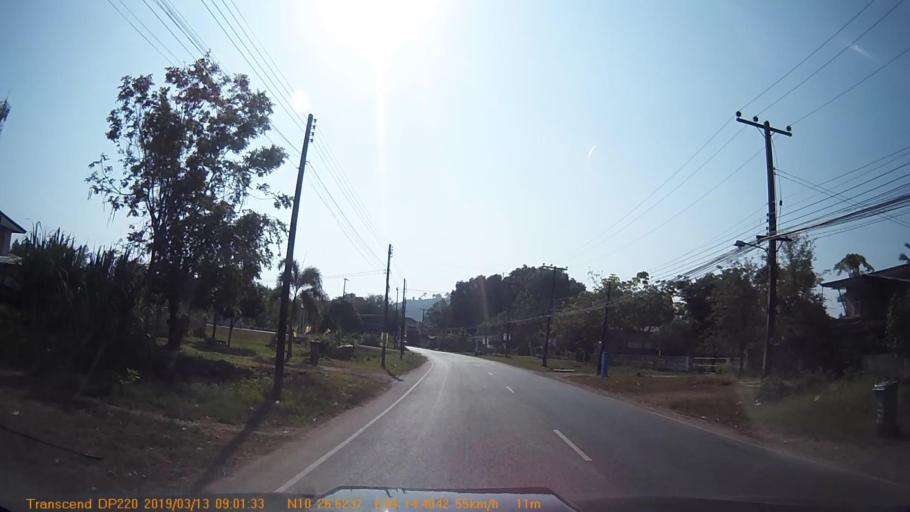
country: TH
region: Chumphon
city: Chumphon
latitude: 10.4436
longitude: 99.2403
